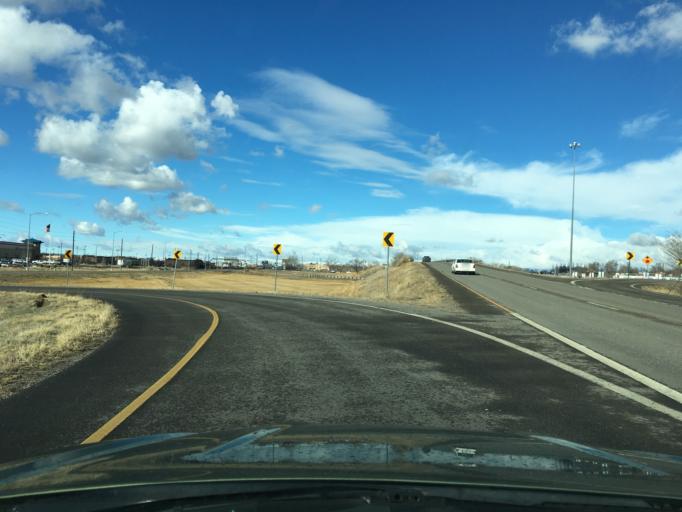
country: US
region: Colorado
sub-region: Mesa County
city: Grand Junction
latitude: 39.0759
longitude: -108.5755
